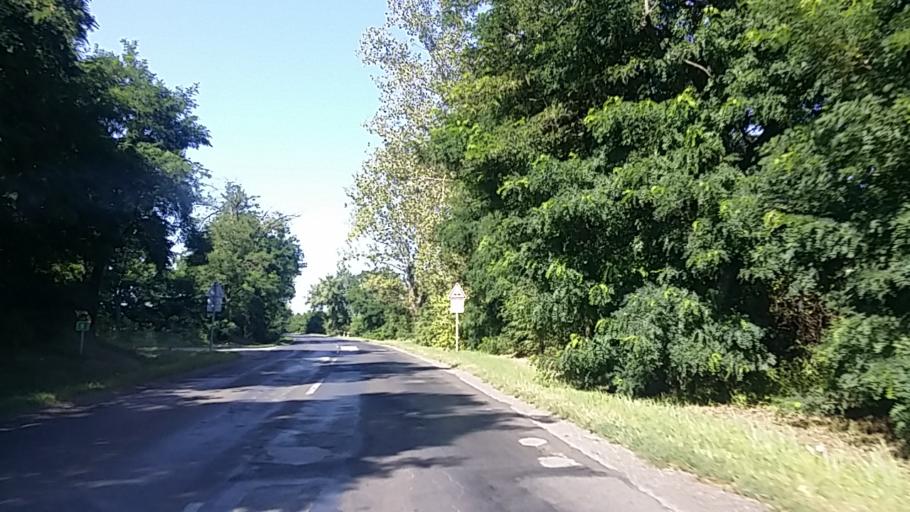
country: HU
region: Fejer
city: Mezofalva
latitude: 46.9434
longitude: 18.8143
